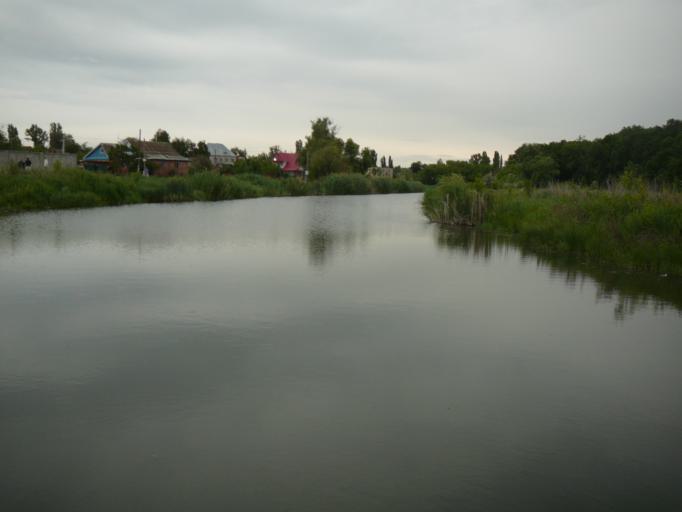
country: RU
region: Saratov
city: Engel's
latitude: 51.4738
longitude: 46.0945
